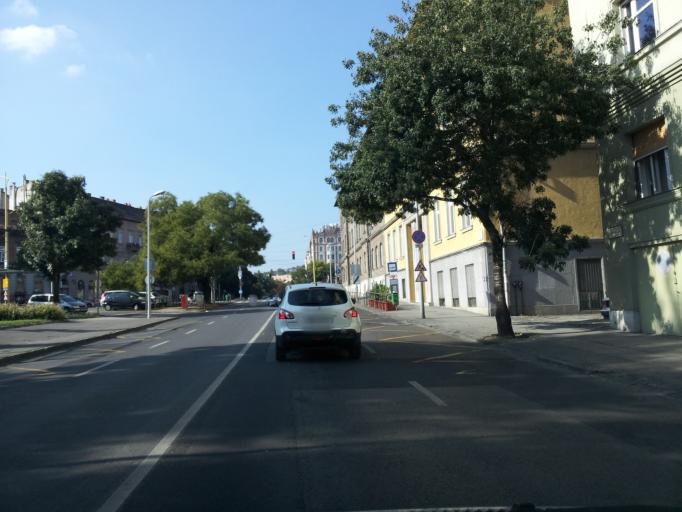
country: HU
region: Budapest
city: Budapest II. keruelet
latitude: 47.5041
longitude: 19.0252
